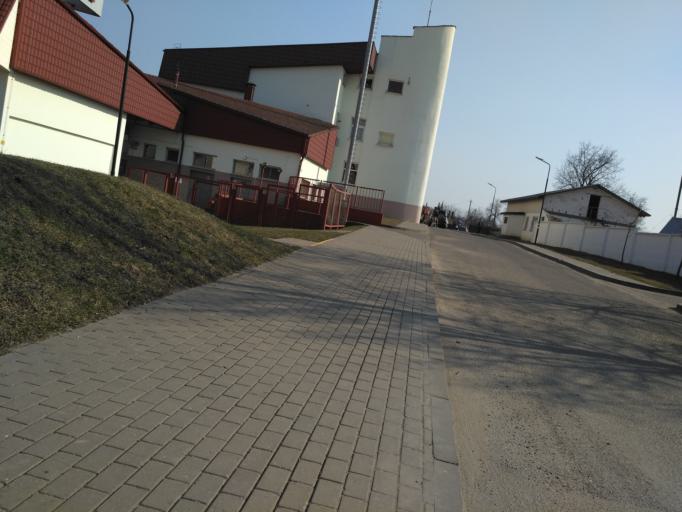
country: BY
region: Minsk
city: Zaslawye
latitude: 54.0093
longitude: 27.2830
